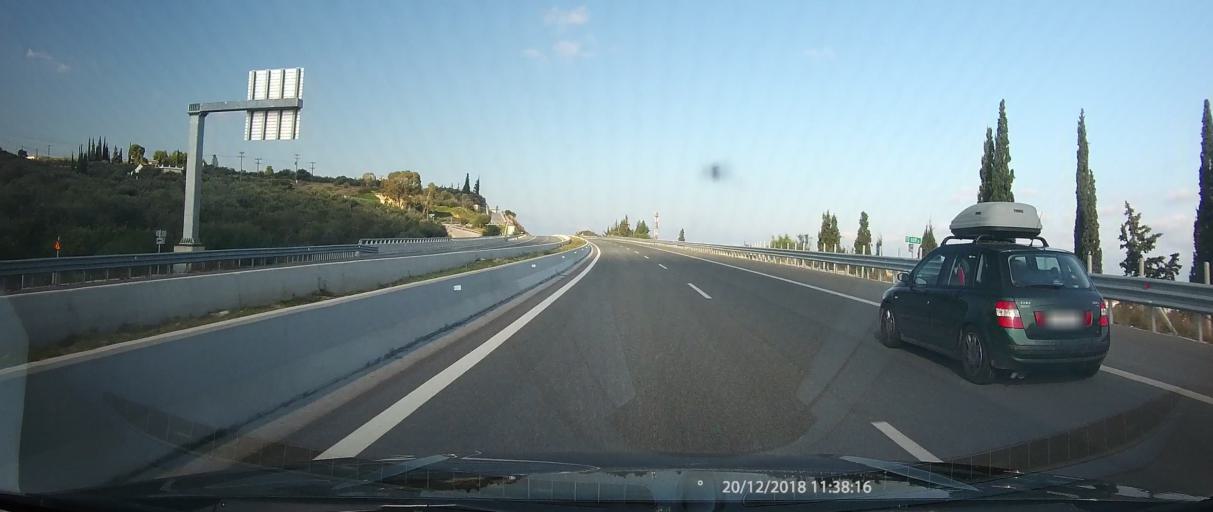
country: GR
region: Peloponnese
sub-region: Nomos Korinthias
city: Kato Dhiminio
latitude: 38.0224
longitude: 22.7273
